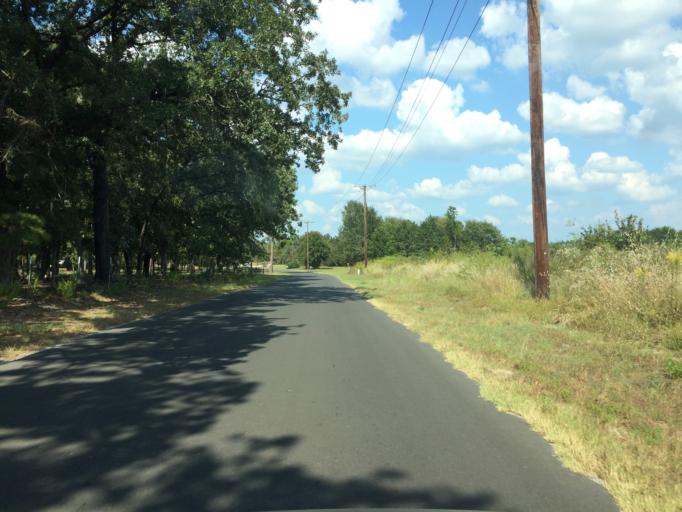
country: US
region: Texas
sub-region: Wood County
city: Hawkins
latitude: 32.6763
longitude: -95.2008
